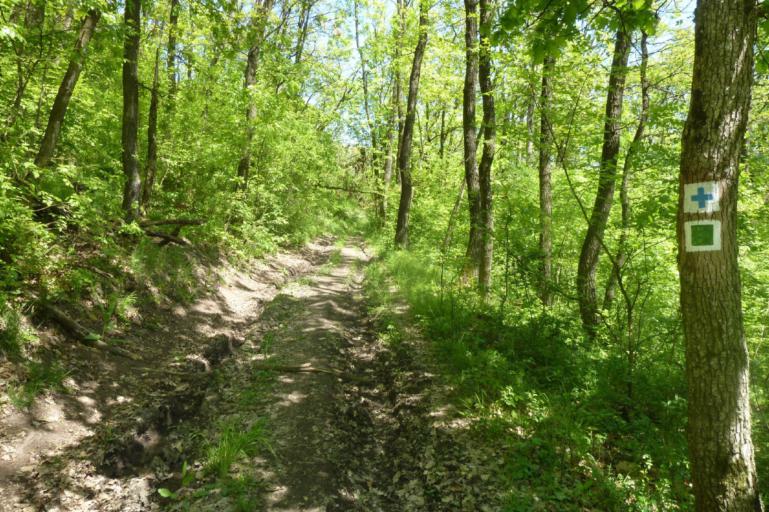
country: HU
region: Pest
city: Szob
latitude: 47.8737
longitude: 18.8295
